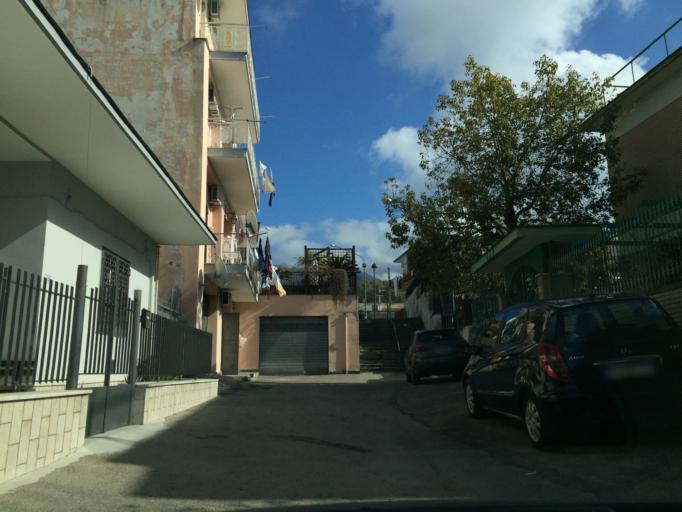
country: IT
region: Campania
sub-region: Provincia di Napoli
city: Massa di Somma
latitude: 40.8481
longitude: 14.3693
